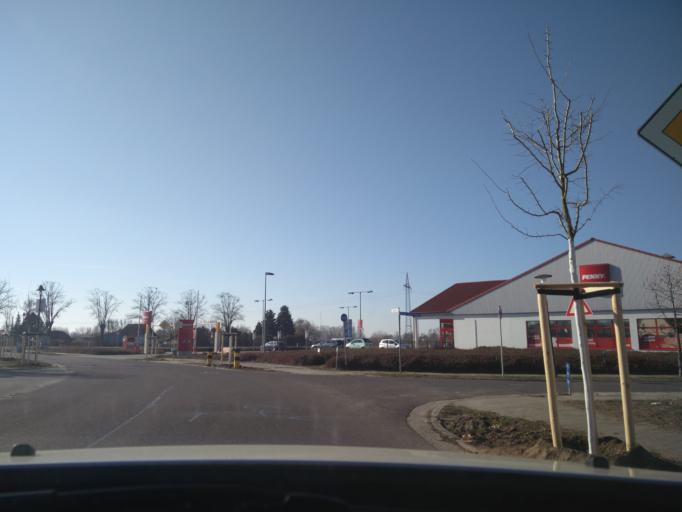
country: DE
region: Brandenburg
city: Brieselang
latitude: 52.5750
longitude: 12.9780
